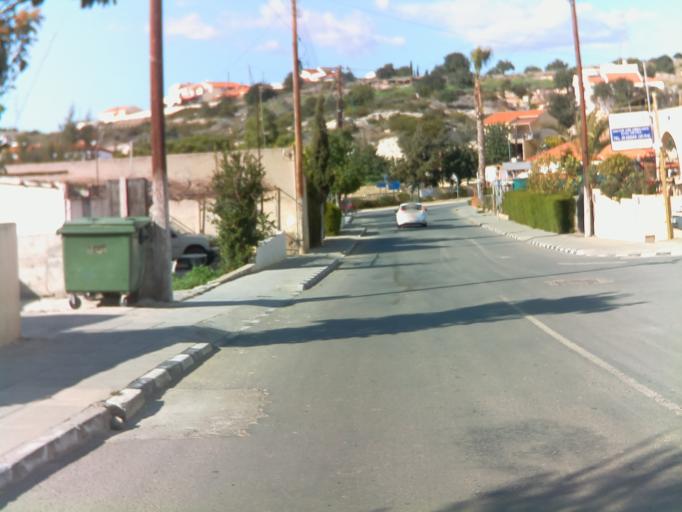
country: CY
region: Limassol
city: Pissouri
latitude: 34.6753
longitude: 32.6995
